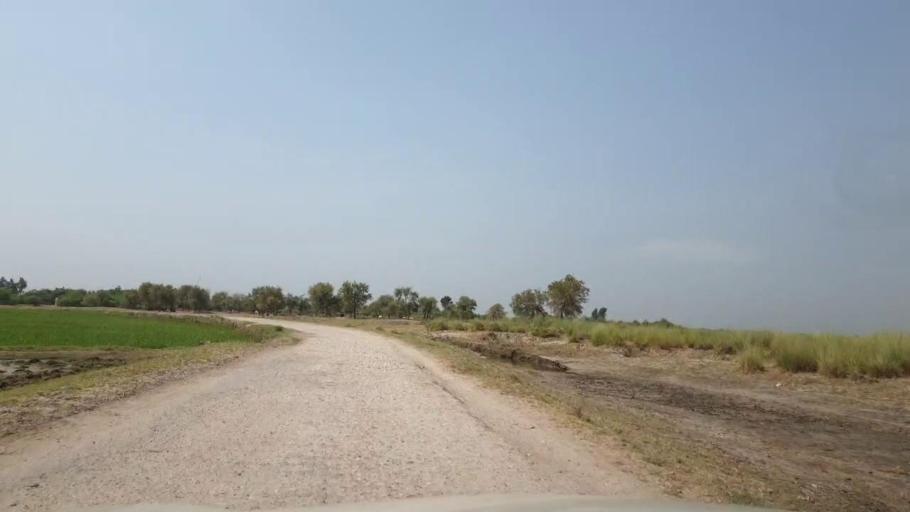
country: PK
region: Sindh
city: Ratodero
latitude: 27.8444
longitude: 68.2637
